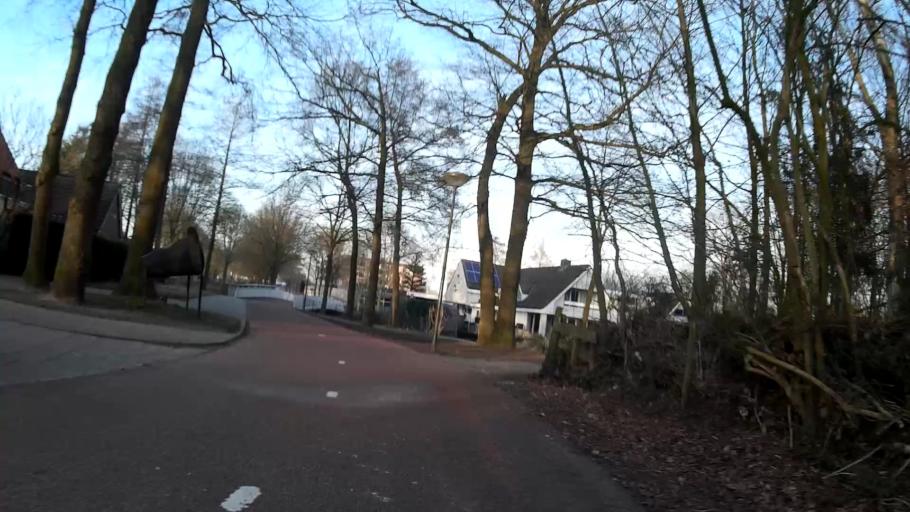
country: NL
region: Utrecht
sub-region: Gemeente Veenendaal
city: Veenendaal
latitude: 52.0257
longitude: 5.5294
